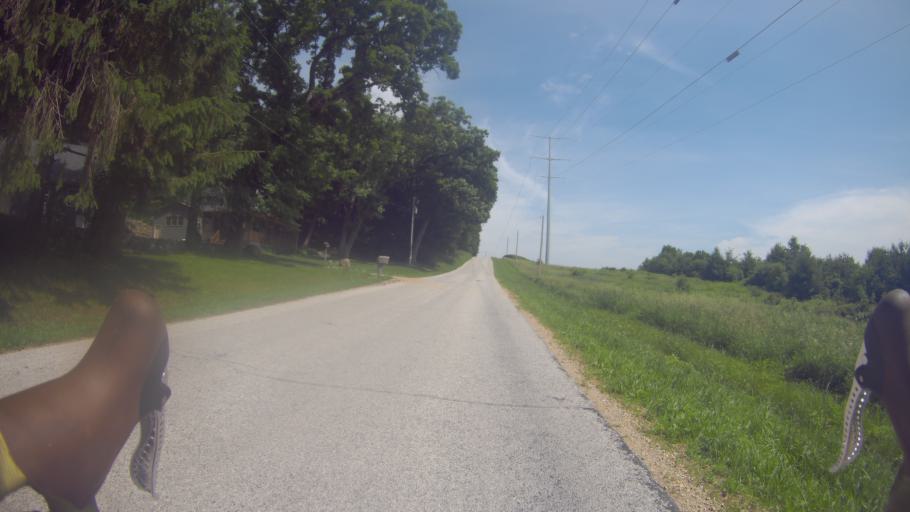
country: US
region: Wisconsin
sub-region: Dane County
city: Deerfield
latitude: 43.0512
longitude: -89.0412
